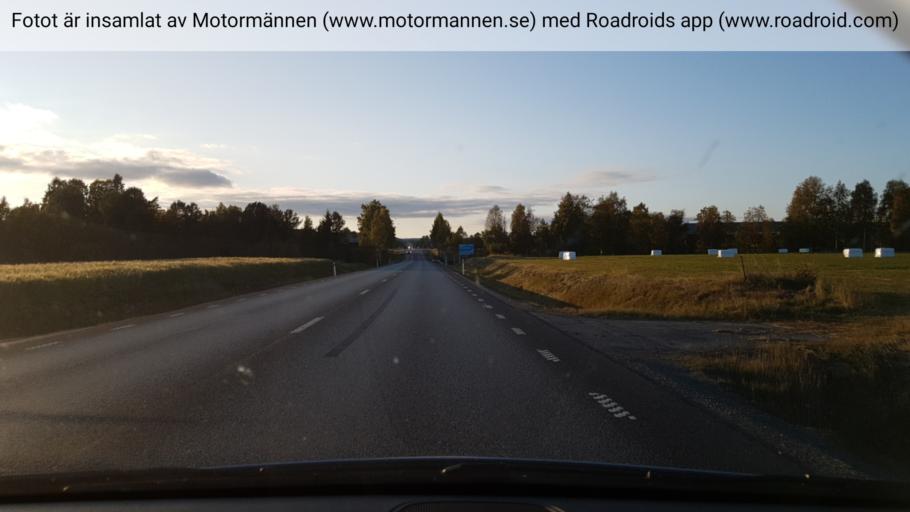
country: SE
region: Vaesterbotten
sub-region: Umea Kommun
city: Roback
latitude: 63.8716
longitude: 20.0713
